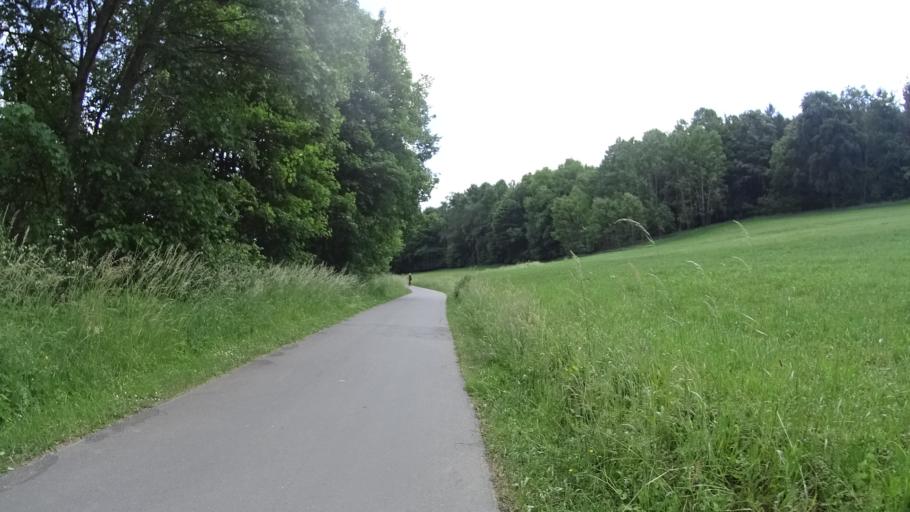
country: DE
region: Bavaria
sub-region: Regierungsbezirk Unterfranken
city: Neunkirchen
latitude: 49.6763
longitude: 9.3666
